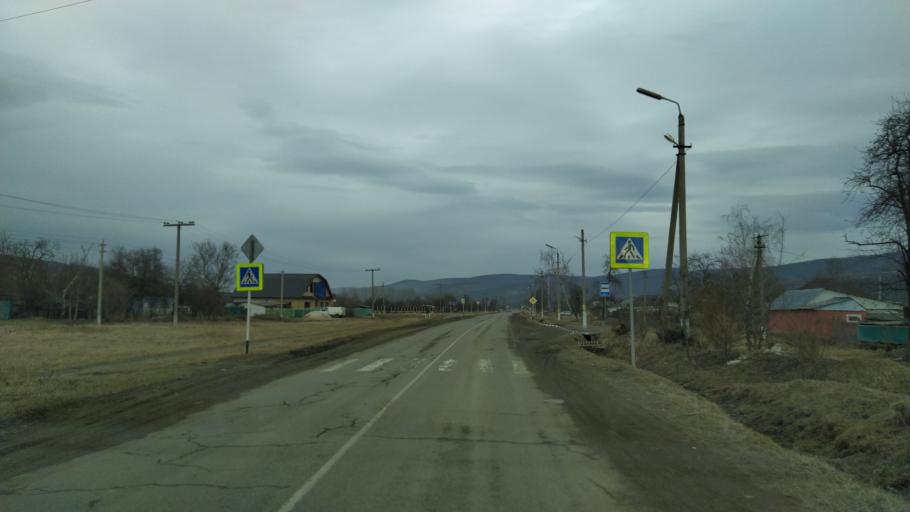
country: RU
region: Krasnodarskiy
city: Peredovaya
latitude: 44.1285
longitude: 41.4837
